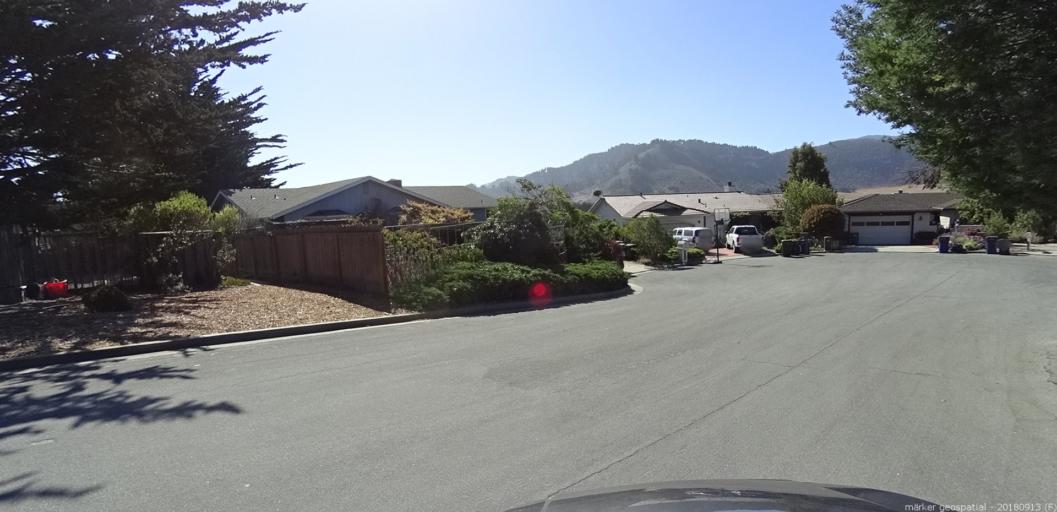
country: US
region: California
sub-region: Monterey County
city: Carmel-by-the-Sea
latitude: 36.5449
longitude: -121.9043
